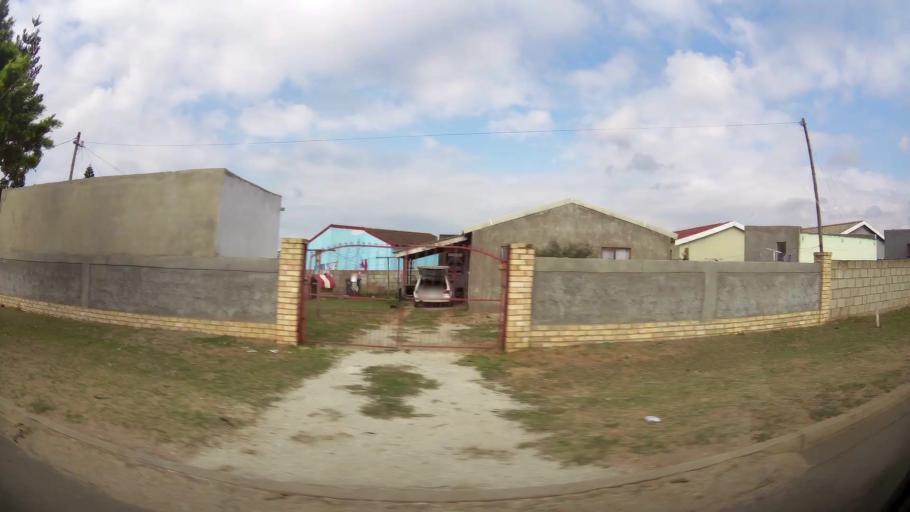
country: ZA
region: Eastern Cape
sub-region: Nelson Mandela Bay Metropolitan Municipality
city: Port Elizabeth
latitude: -33.8147
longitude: 25.5881
